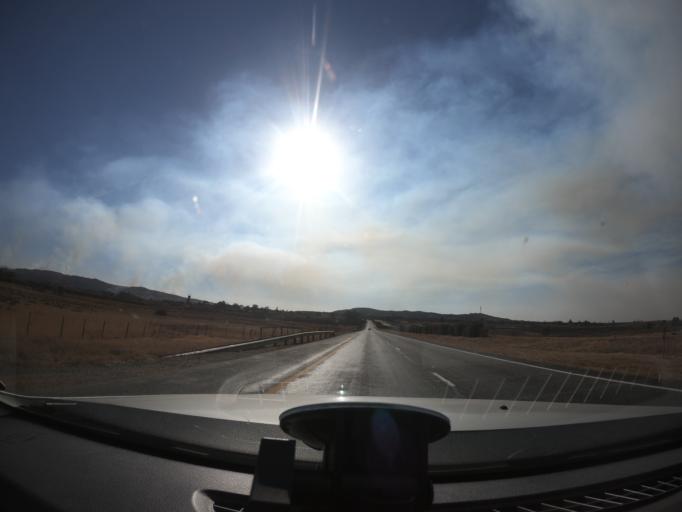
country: ZA
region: Gauteng
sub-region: Sedibeng District Municipality
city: Heidelberg
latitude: -26.5033
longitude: 28.3828
